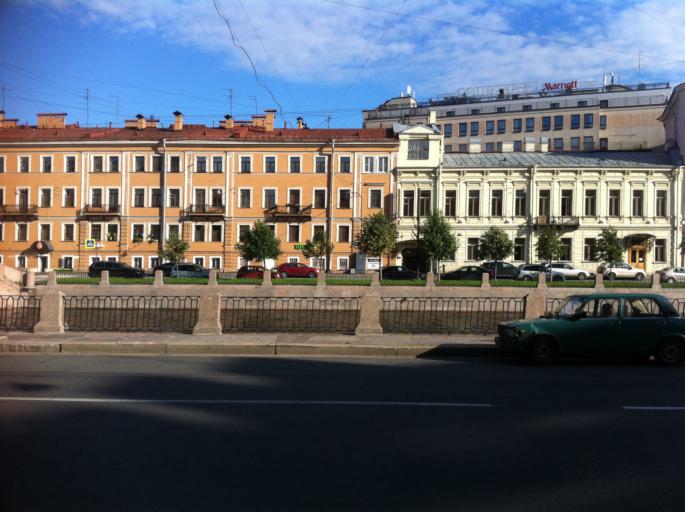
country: RU
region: St.-Petersburg
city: Admiralteisky
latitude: 59.9196
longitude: 30.2839
